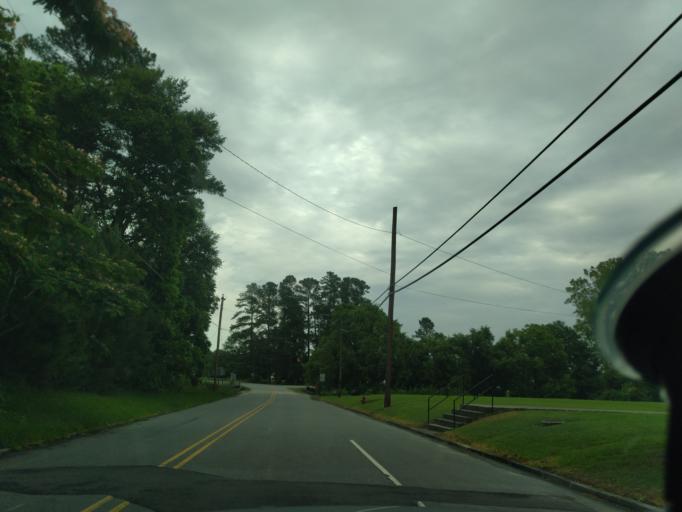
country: US
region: North Carolina
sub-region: Washington County
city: Plymouth
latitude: 35.8800
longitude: -76.6119
